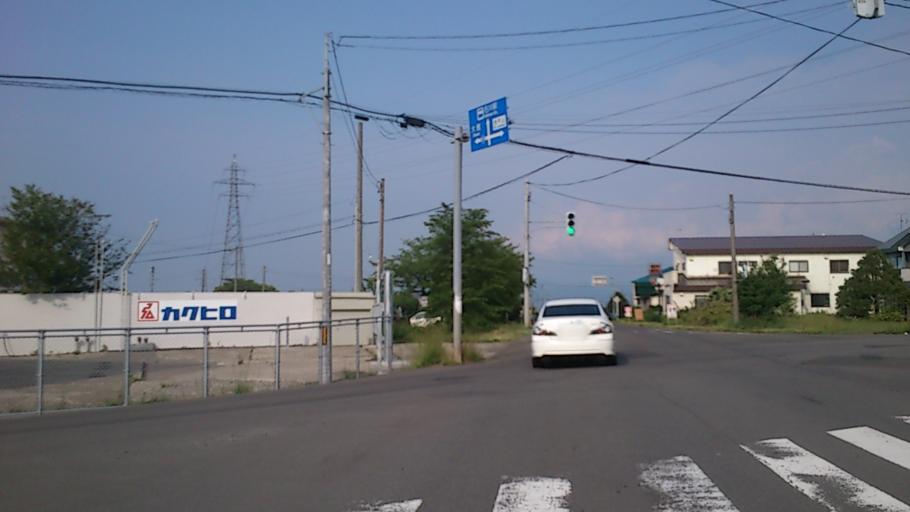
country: JP
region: Aomori
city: Hirosaki
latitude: 40.5592
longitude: 140.4905
